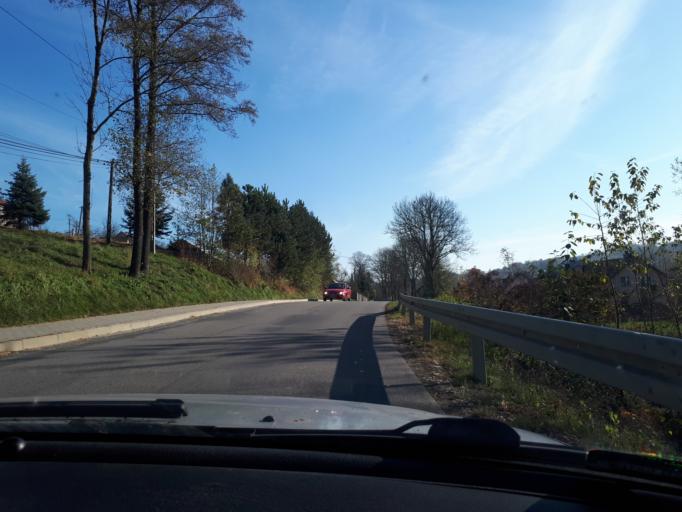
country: PL
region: Subcarpathian Voivodeship
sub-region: Powiat debicki
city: Debica
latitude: 50.0002
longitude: 21.4135
